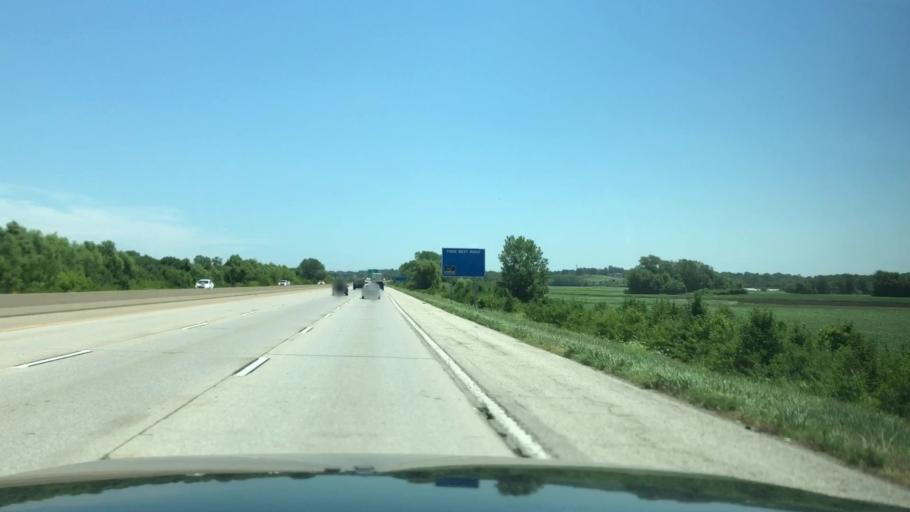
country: US
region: Missouri
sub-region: Saint Louis County
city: Bridgeton
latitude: 38.7912
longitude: -90.4401
